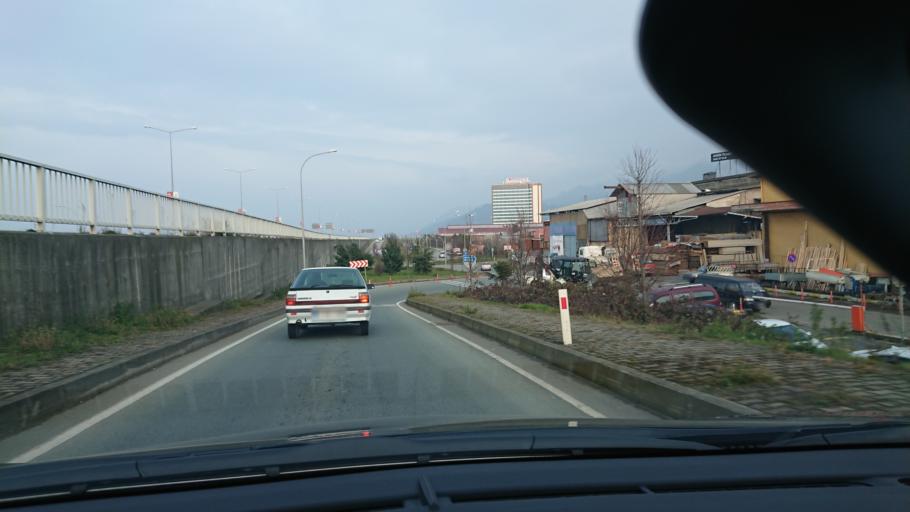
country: TR
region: Rize
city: Gundogdu
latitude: 41.0448
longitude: 40.5757
